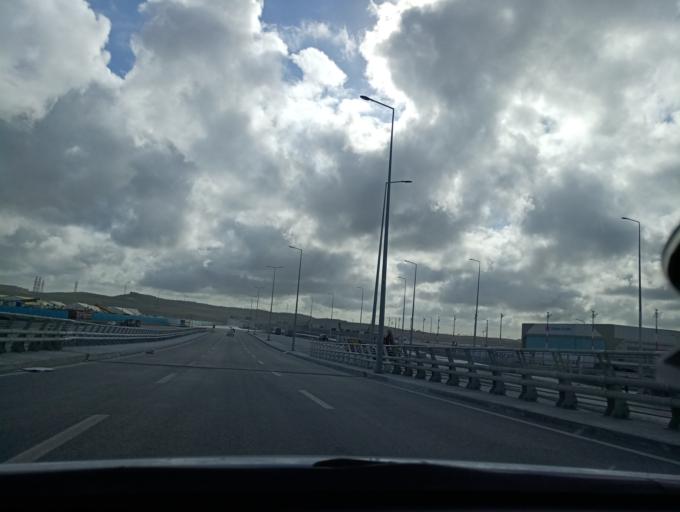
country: TR
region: Istanbul
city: Durusu
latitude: 41.2562
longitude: 28.7388
